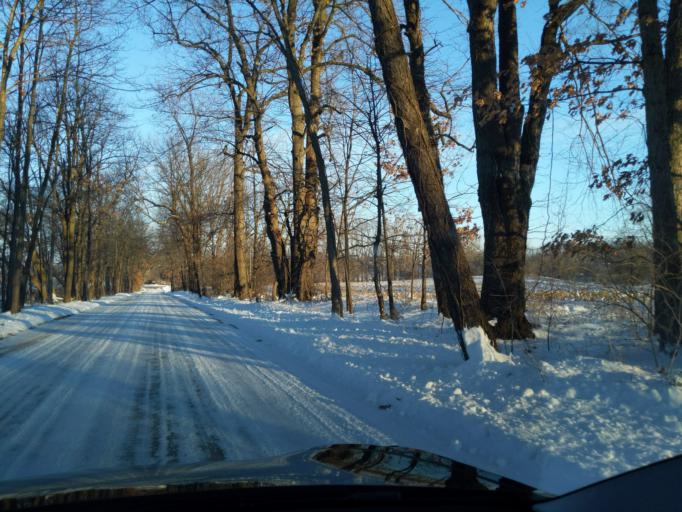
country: US
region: Michigan
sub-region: Ingham County
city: Stockbridge
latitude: 42.5343
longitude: -84.1158
